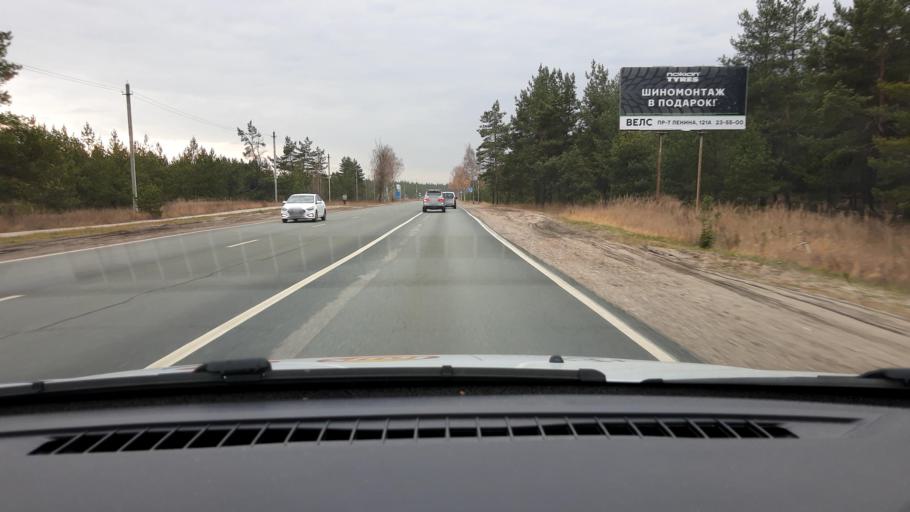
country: RU
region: Nizjnij Novgorod
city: Dzerzhinsk
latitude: 56.2806
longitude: 43.4752
